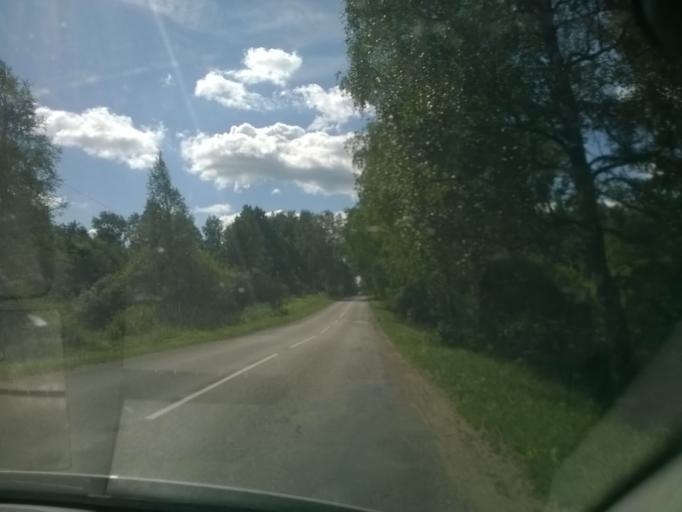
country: LV
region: Aluksnes Rajons
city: Aluksne
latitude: 57.4434
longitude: 27.0360
